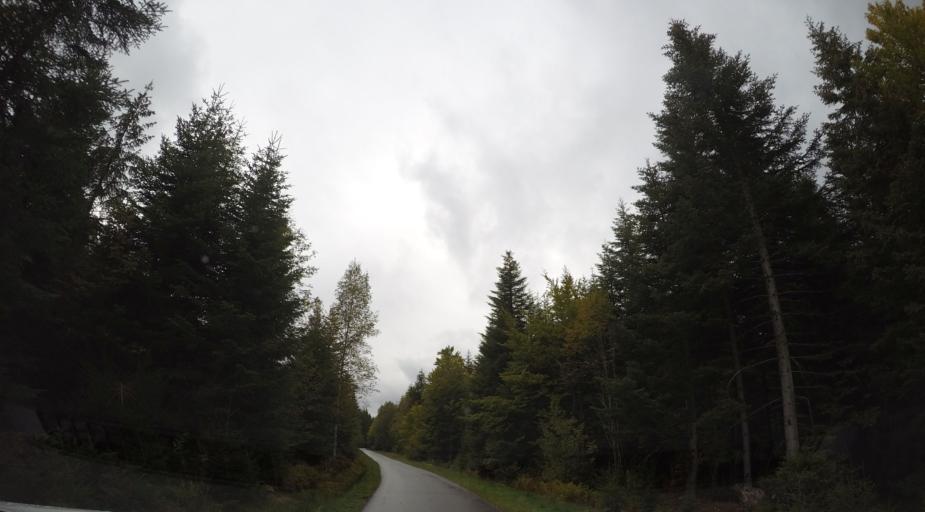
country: DE
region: Baden-Wuerttemberg
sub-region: Karlsruhe Region
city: Baiersbronn
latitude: 48.4795
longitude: 8.3132
